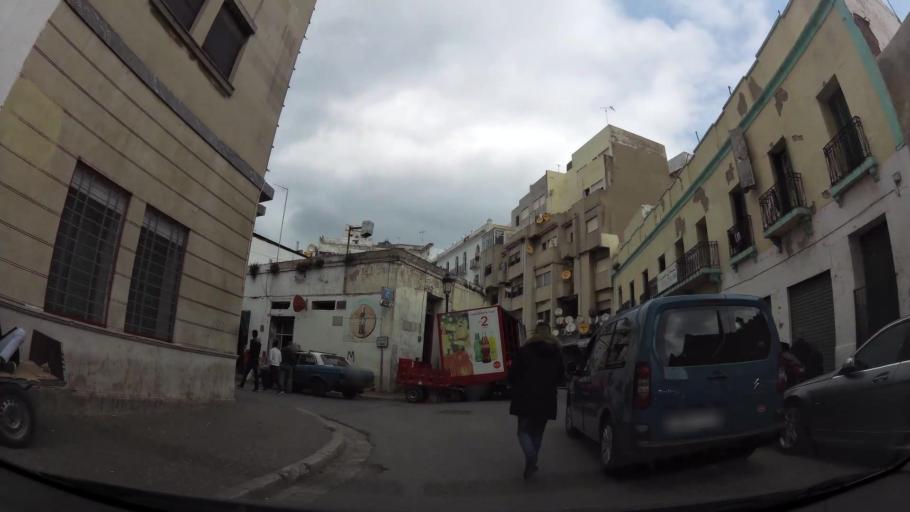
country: MA
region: Tanger-Tetouan
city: Tetouan
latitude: 35.5689
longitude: -5.3694
